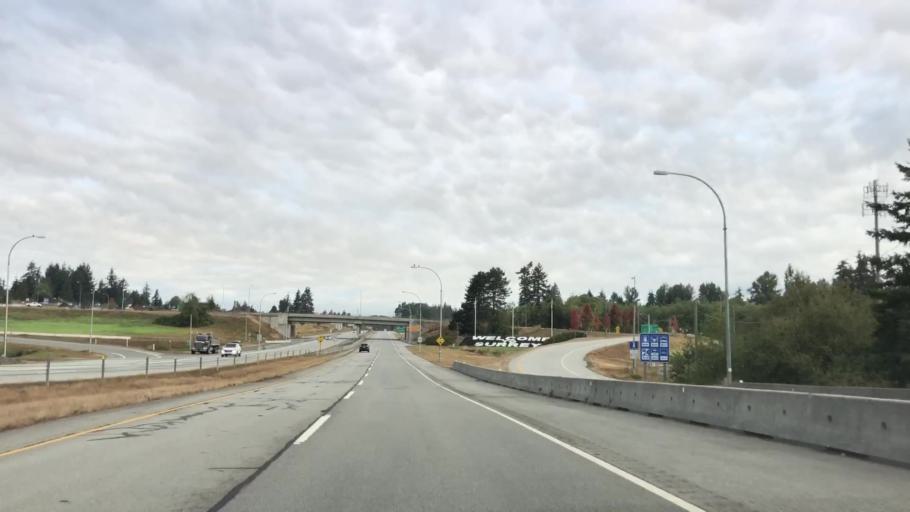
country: US
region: Washington
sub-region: Whatcom County
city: Blaine
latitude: 49.0141
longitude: -122.7579
